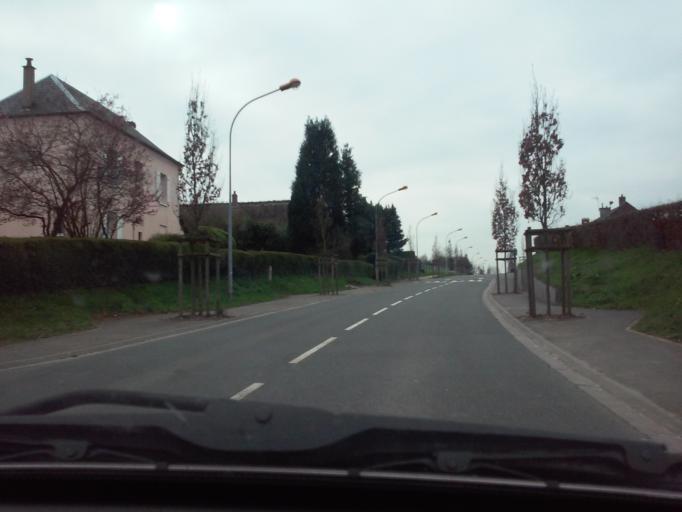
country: FR
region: Haute-Normandie
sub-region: Departement de la Seine-Maritime
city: Saint-Arnoult
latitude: 49.5279
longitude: 0.6688
